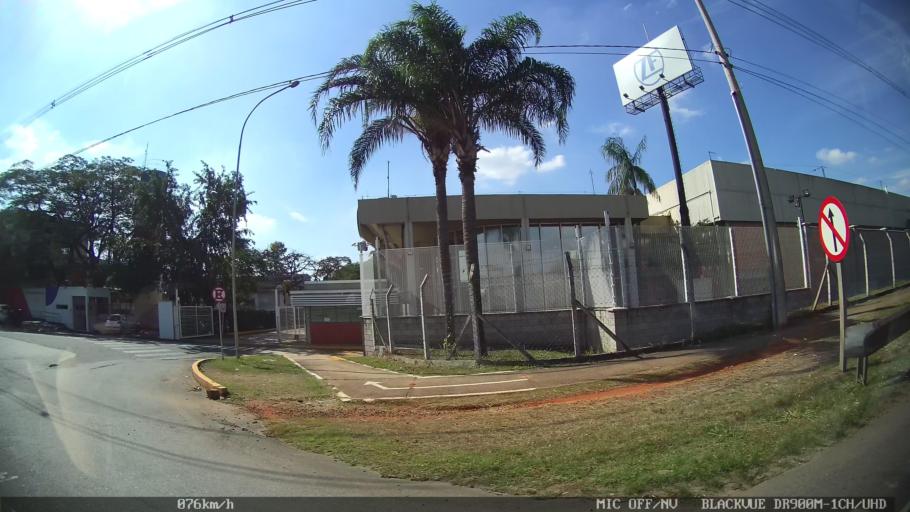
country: BR
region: Sao Paulo
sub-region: Hortolandia
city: Hortolandia
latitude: -22.8460
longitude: -47.1637
